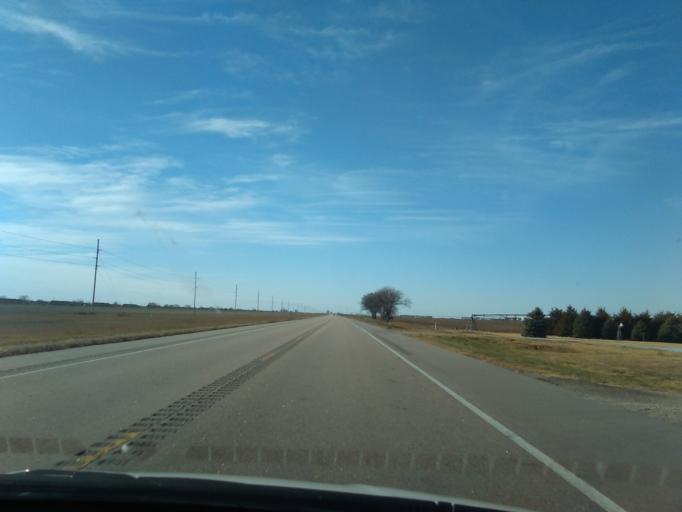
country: US
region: Nebraska
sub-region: Clay County
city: Harvard
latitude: 40.5828
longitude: -98.1735
